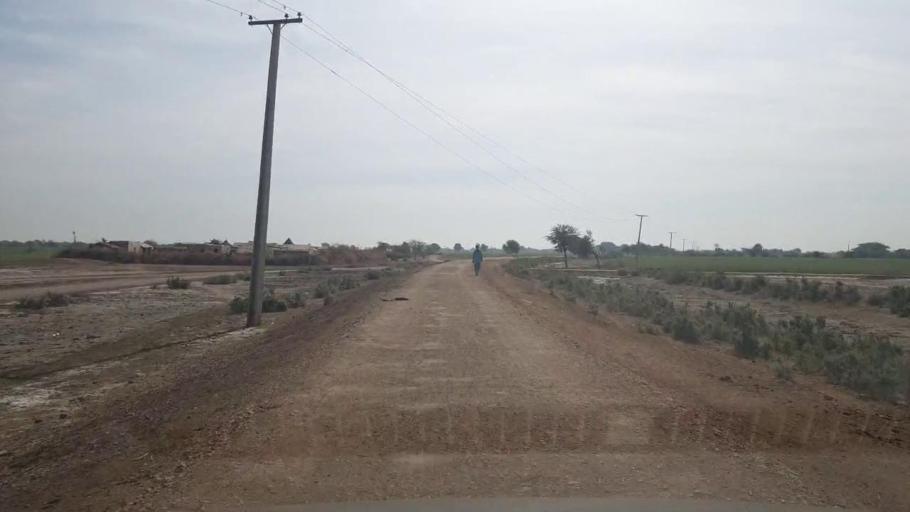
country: PK
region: Sindh
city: Umarkot
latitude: 25.3631
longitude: 69.6247
